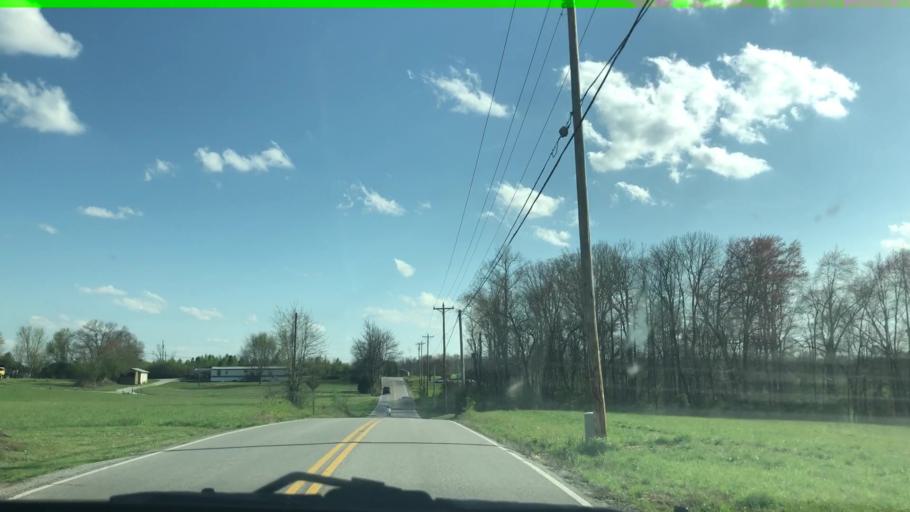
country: US
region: Tennessee
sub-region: Putnam County
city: Baxter
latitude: 36.0848
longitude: -85.5847
